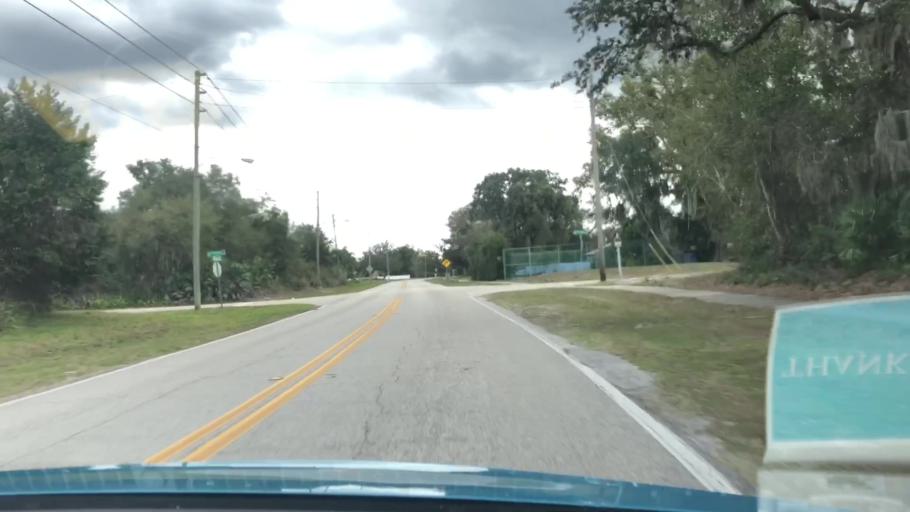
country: US
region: Florida
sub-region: Volusia County
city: Deltona
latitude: 28.8806
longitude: -81.2212
